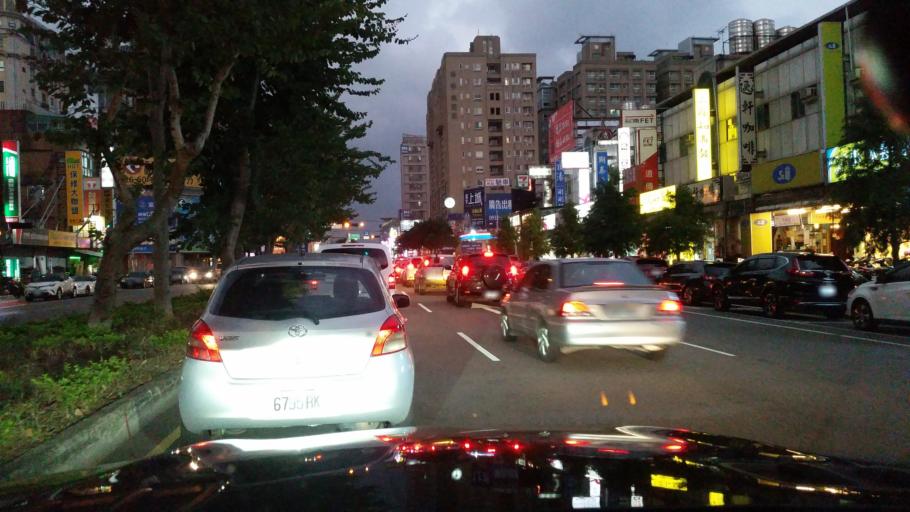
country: TW
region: Taiwan
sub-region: Taoyuan
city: Taoyuan
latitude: 25.0565
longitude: 121.3634
